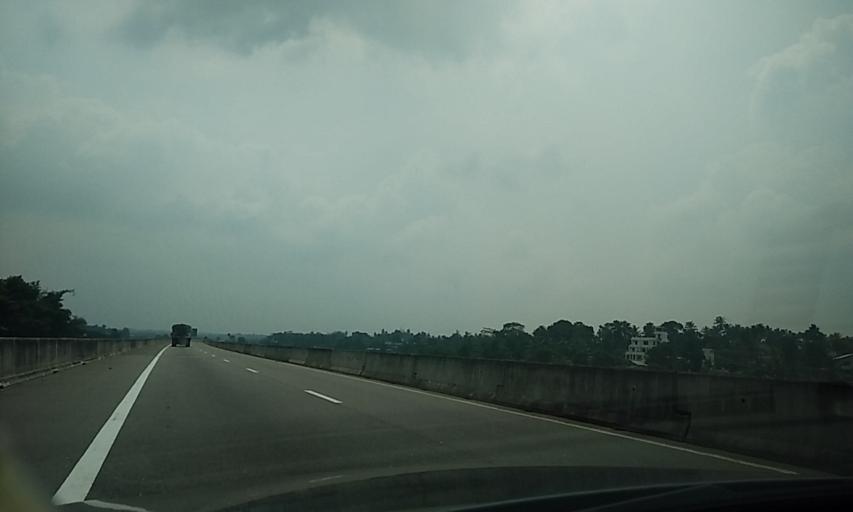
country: LK
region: Western
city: Homagama
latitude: 6.8991
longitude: 79.9794
